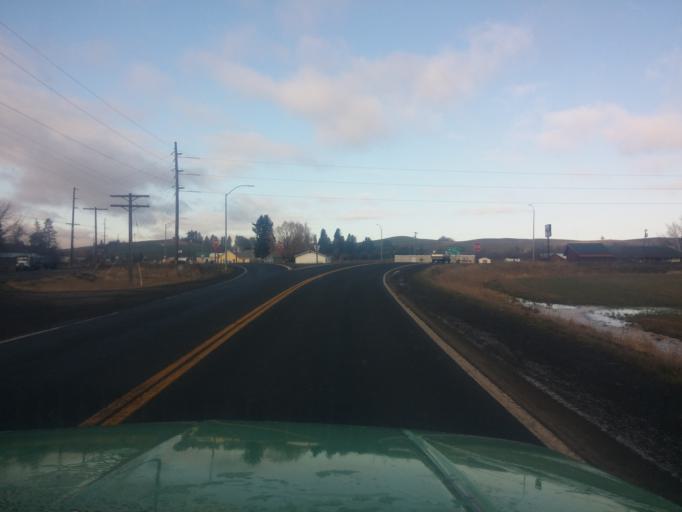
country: US
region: Idaho
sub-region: Latah County
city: Moscow
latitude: 46.9293
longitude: -116.9310
